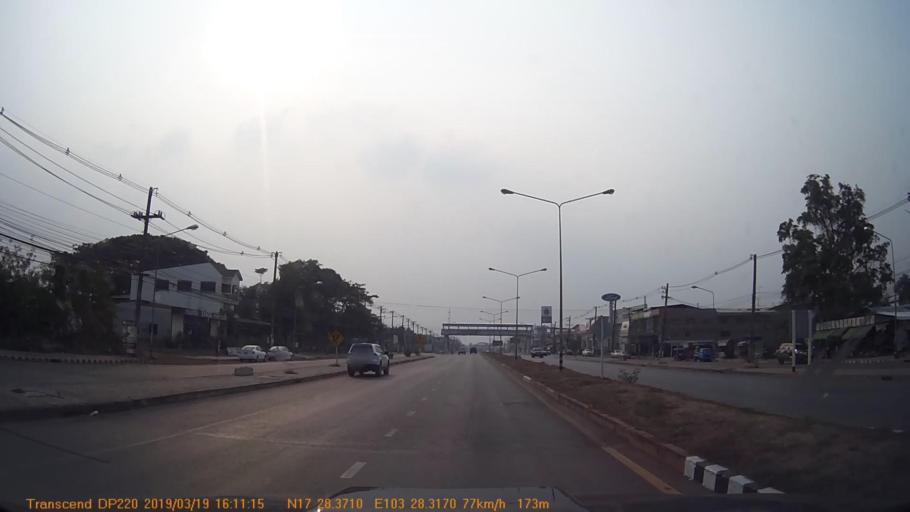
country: TH
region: Sakon Nakhon
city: Sawang Daen Din
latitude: 17.4730
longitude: 103.4713
